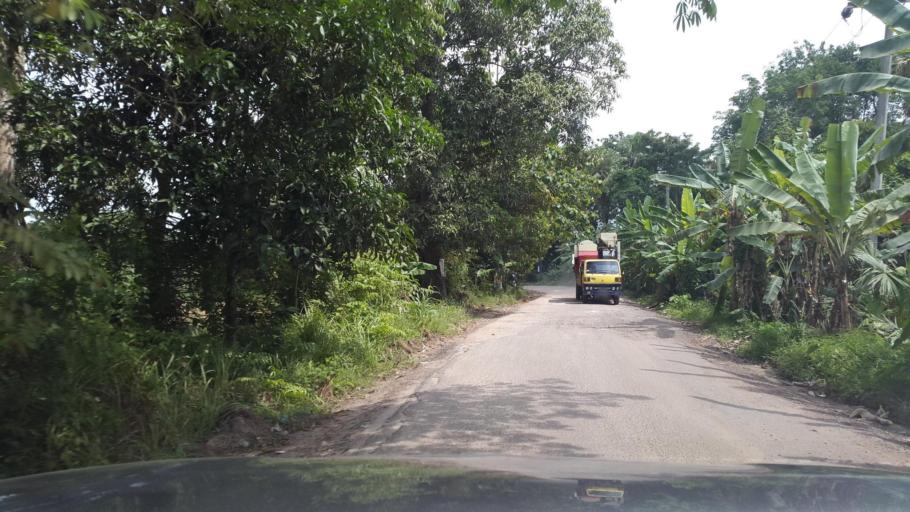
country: ID
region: South Sumatra
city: Tanjung Lubuk
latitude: -3.2692
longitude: 104.8723
